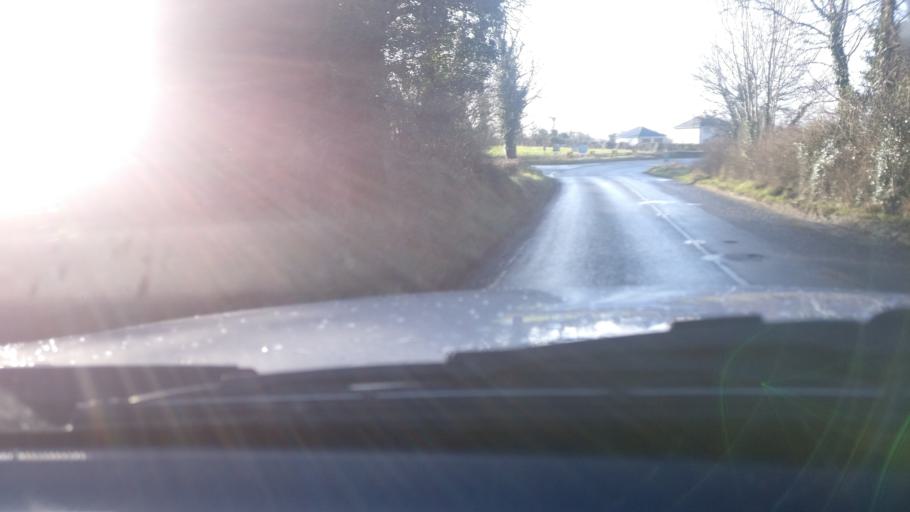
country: IE
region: Ulster
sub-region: An Cabhan
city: Ballyjamesduff
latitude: 53.8593
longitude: -7.2194
